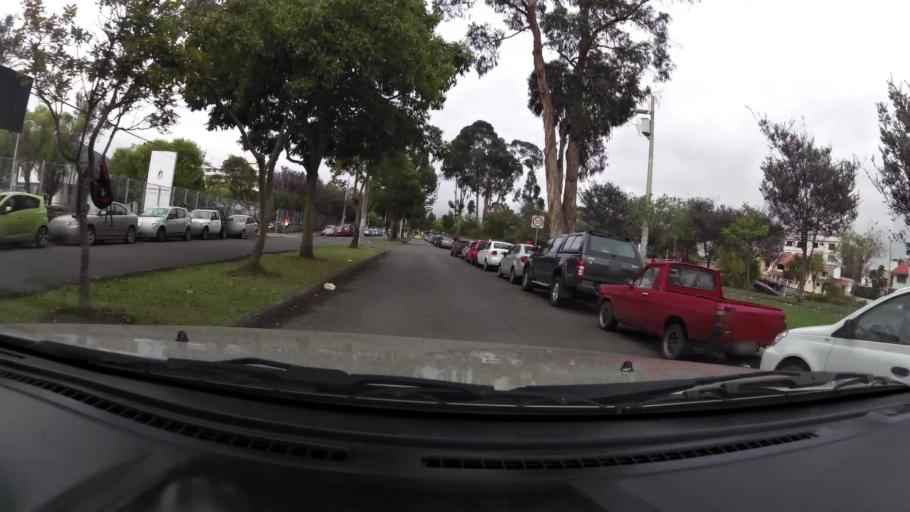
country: EC
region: Azuay
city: Cuenca
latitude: -2.9093
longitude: -78.9910
